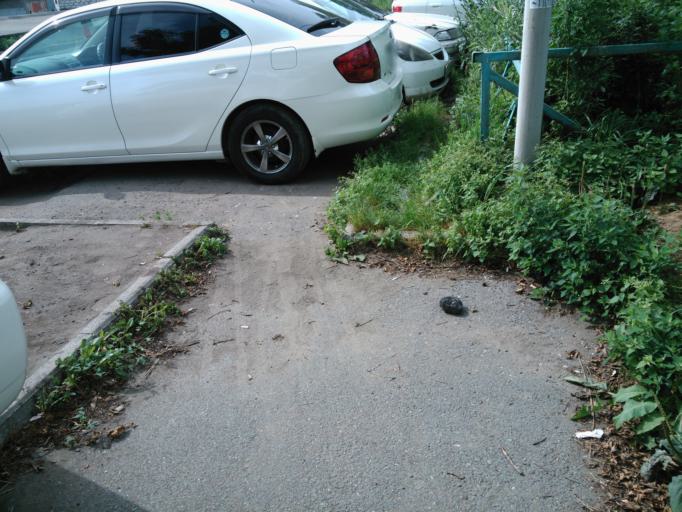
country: RU
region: Primorskiy
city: Vladivostok
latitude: 43.0919
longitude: 131.9770
